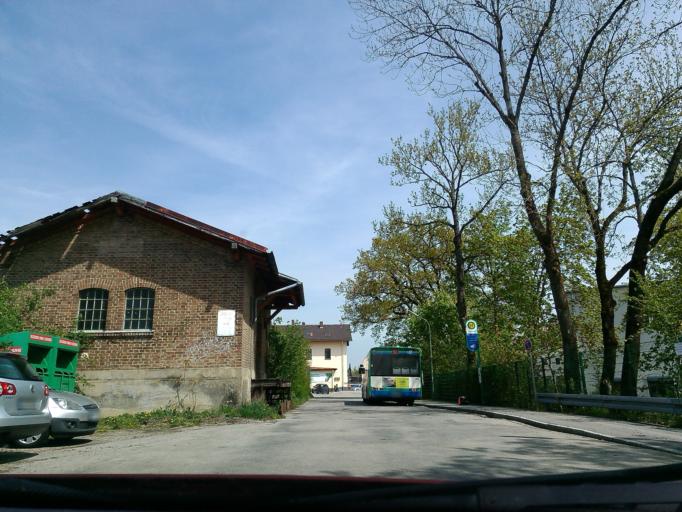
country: DE
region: Bavaria
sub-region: Upper Bavaria
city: Gauting
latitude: 48.0695
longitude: 11.3760
